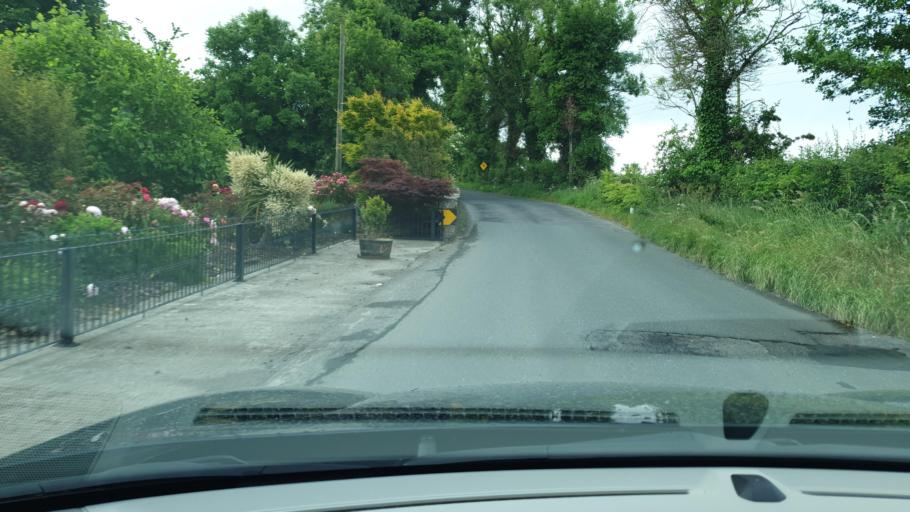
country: IE
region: Leinster
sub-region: An Mhi
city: Ashbourne
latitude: 53.5401
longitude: -6.4079
